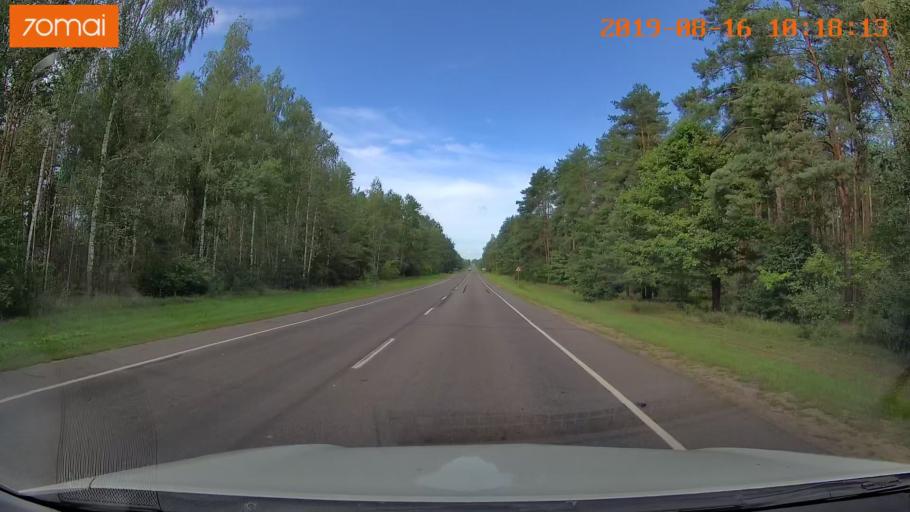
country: BY
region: Mogilev
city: Asipovichy
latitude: 53.3058
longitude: 28.6957
